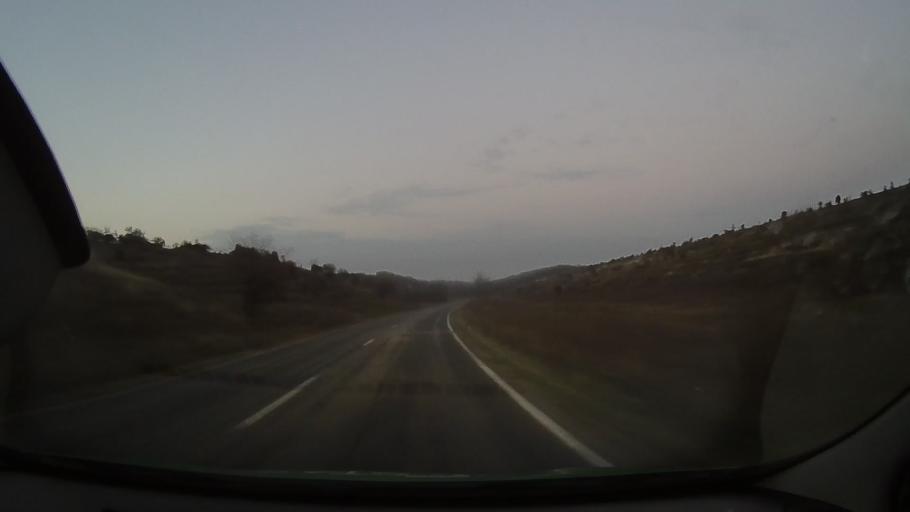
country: RO
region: Constanta
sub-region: Comuna Baneasa
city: Baneasa
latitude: 44.0725
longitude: 27.7363
